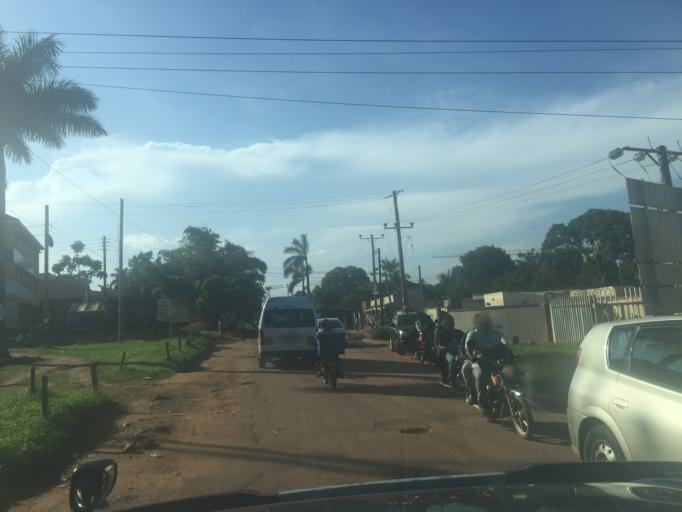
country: UG
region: Central Region
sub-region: Kampala District
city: Kampala
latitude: 0.2979
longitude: 32.5938
